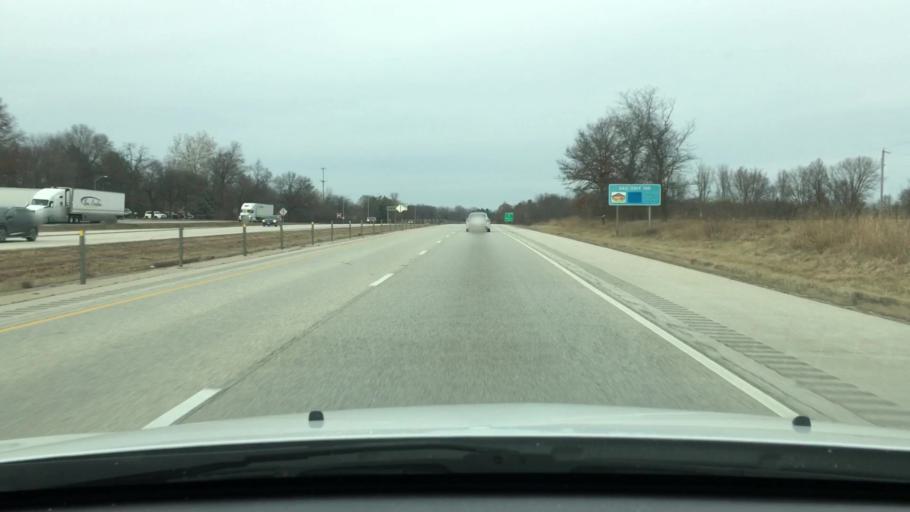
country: US
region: Illinois
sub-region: Sangamon County
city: Sherman
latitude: 39.8861
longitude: -89.5960
